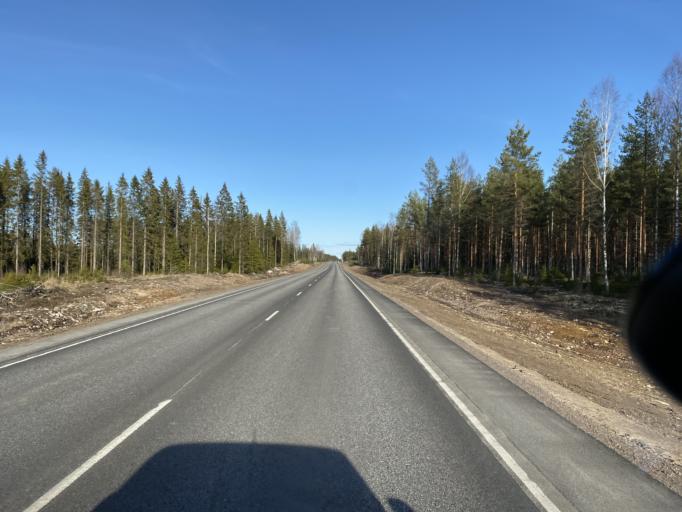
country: FI
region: Satakunta
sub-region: Pori
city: Kokemaeki
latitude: 61.1683
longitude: 22.4491
